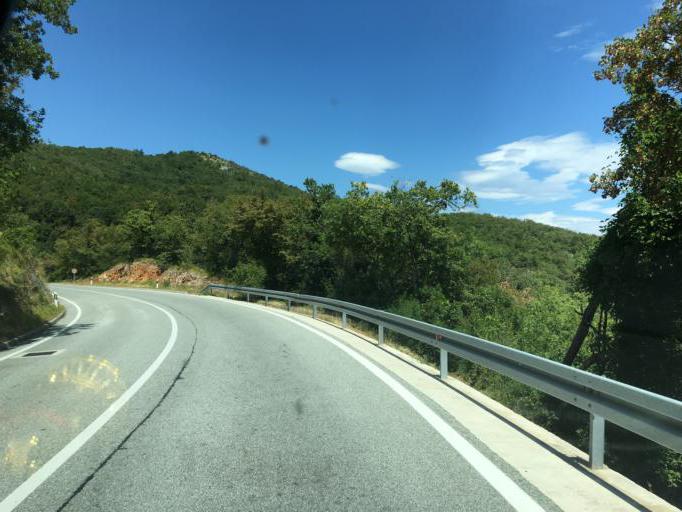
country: HR
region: Istarska
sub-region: Grad Labin
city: Rabac
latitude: 45.1356
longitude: 14.2061
